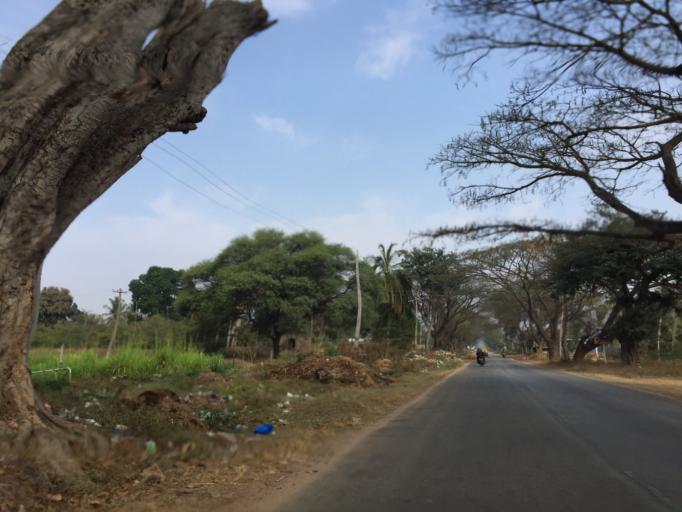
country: IN
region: Karnataka
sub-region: Bangalore Rural
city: Devanhalli
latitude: 13.3302
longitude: 77.6912
